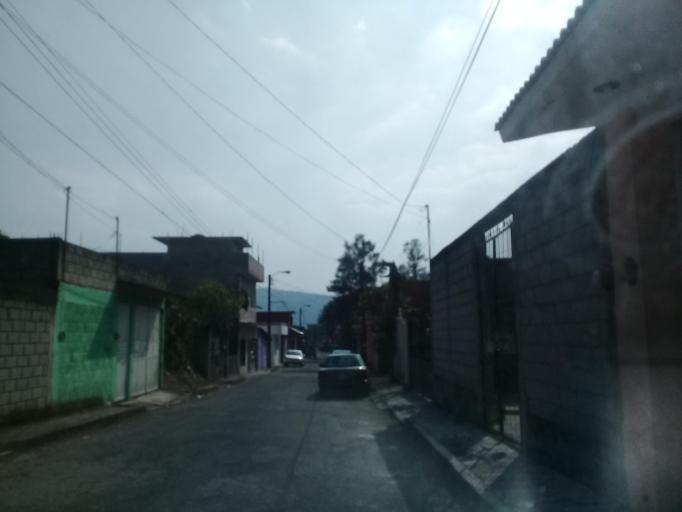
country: MX
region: Veracruz
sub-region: Mariano Escobedo
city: Palmira
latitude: 18.8720
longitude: -97.1036
